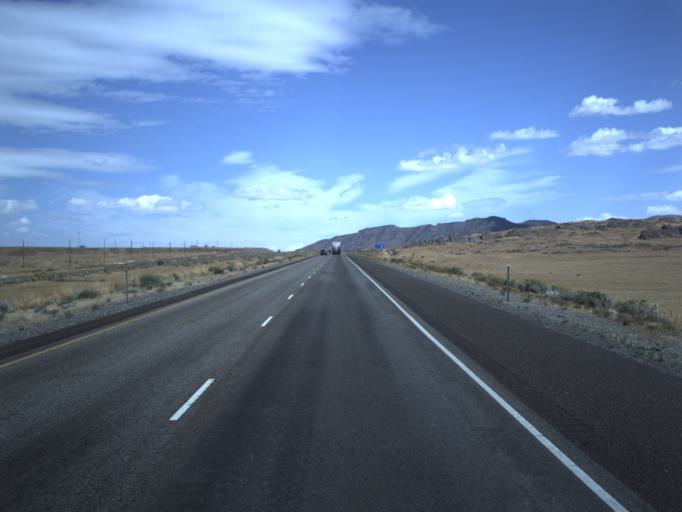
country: US
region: Utah
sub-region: Tooele County
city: Grantsville
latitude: 40.7547
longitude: -113.0292
